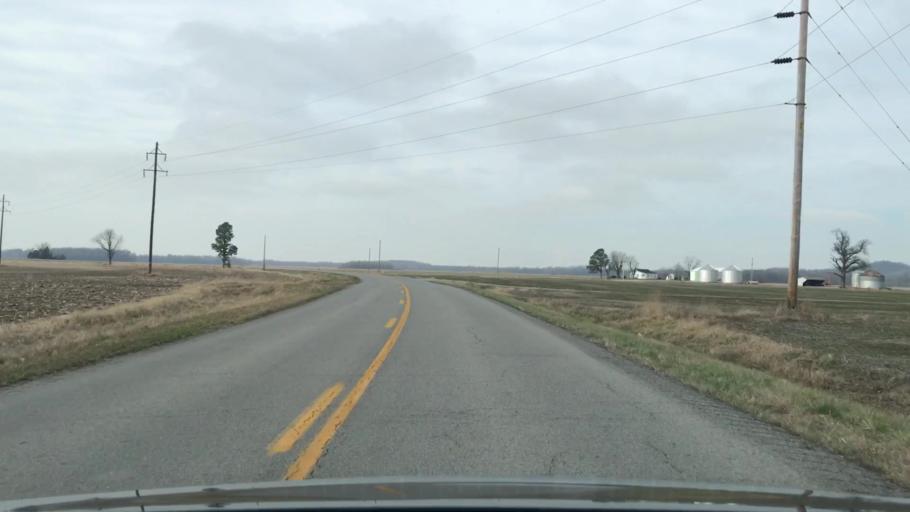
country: US
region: Kentucky
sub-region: McLean County
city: Calhoun
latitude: 37.5336
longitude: -87.3091
